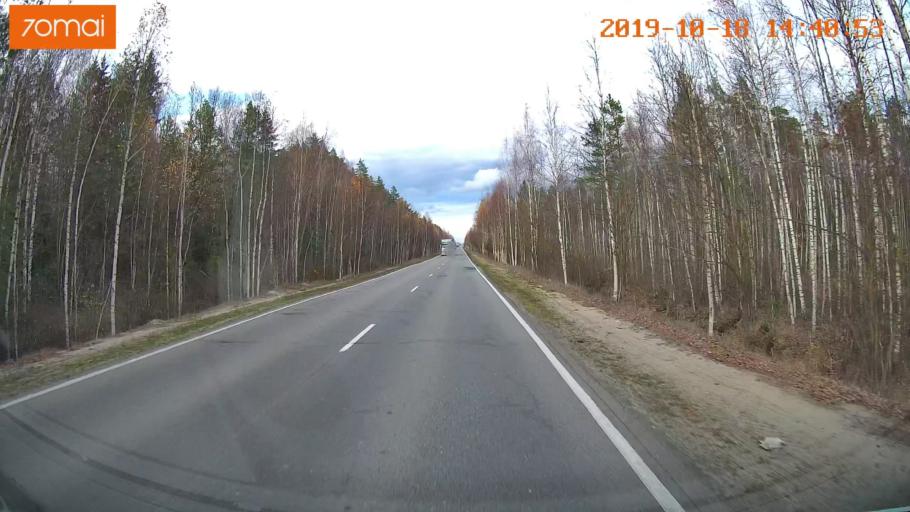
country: RU
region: Vladimir
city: Velikodvorskiy
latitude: 55.2834
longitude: 40.6698
